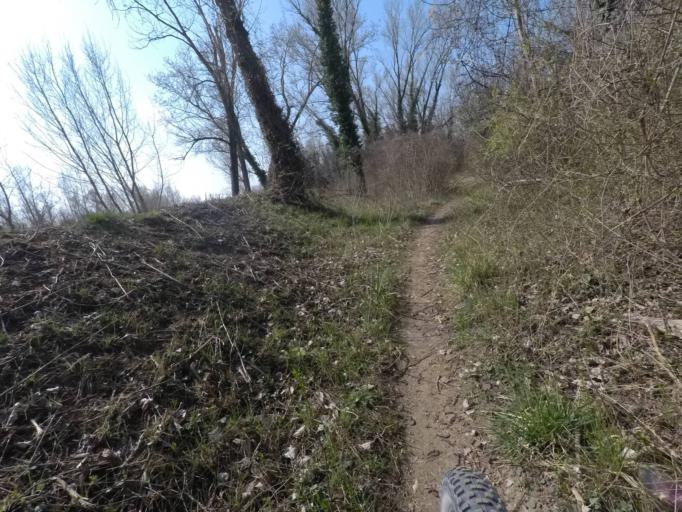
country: IT
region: Friuli Venezia Giulia
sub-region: Provincia di Udine
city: Remanzacco
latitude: 46.0635
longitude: 13.3296
